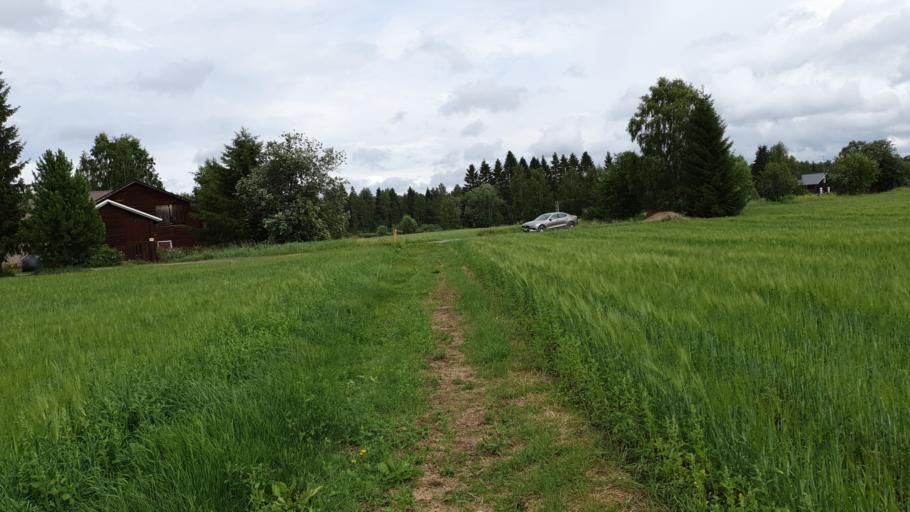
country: FI
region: Kainuu
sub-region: Kehys-Kainuu
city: Kuhmo
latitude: 64.1285
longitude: 29.5693
